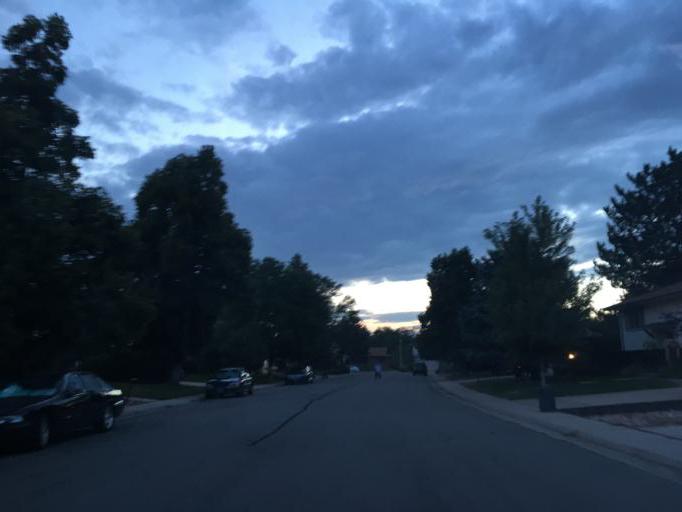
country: US
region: Colorado
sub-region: Adams County
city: Aurora
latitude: 39.6873
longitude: -104.8483
